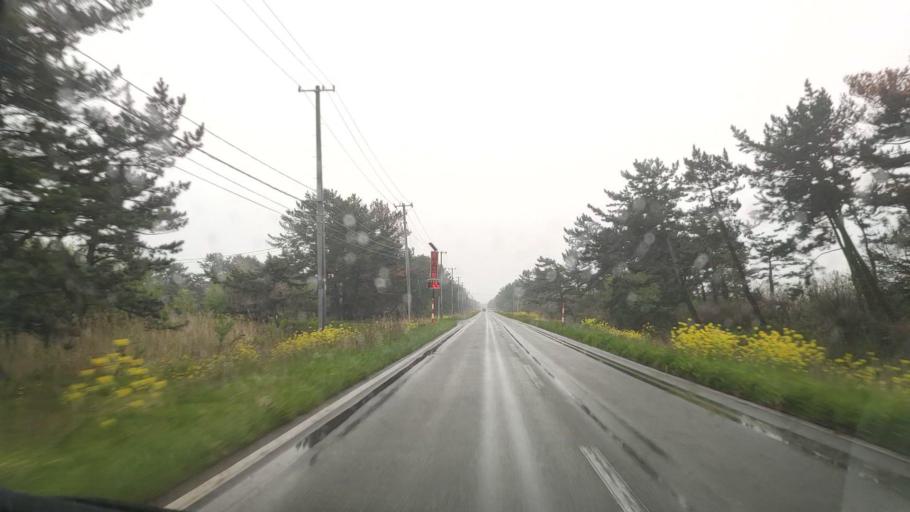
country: JP
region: Akita
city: Tenno
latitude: 40.0289
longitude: 139.9526
